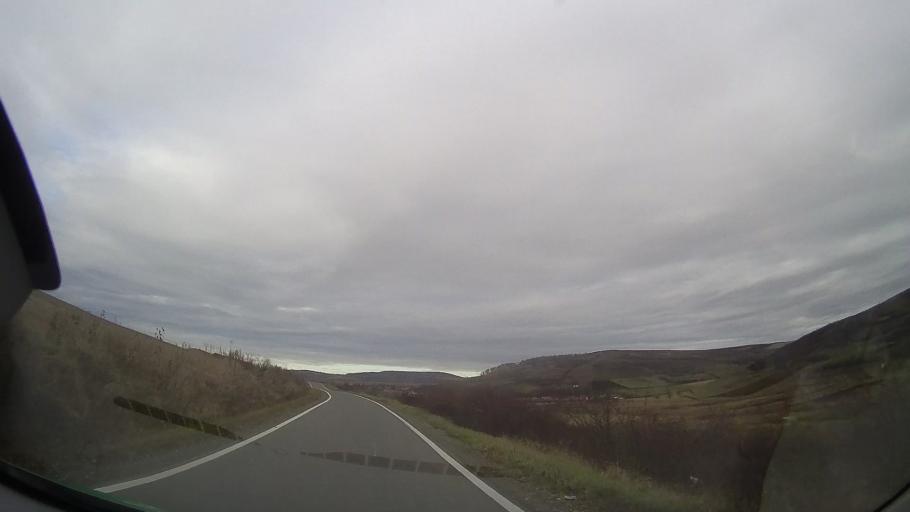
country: RO
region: Mures
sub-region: Comuna Faragau
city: Faragau
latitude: 46.7693
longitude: 24.5577
